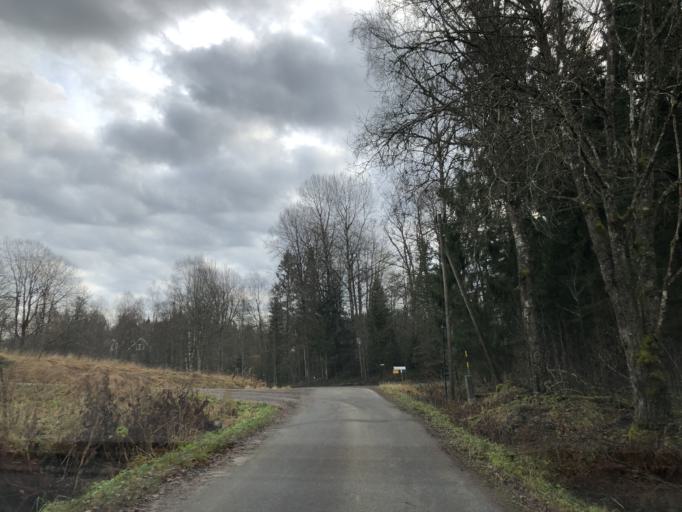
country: SE
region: Vaestra Goetaland
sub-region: Ulricehamns Kommun
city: Ulricehamn
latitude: 57.7268
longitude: 13.3299
